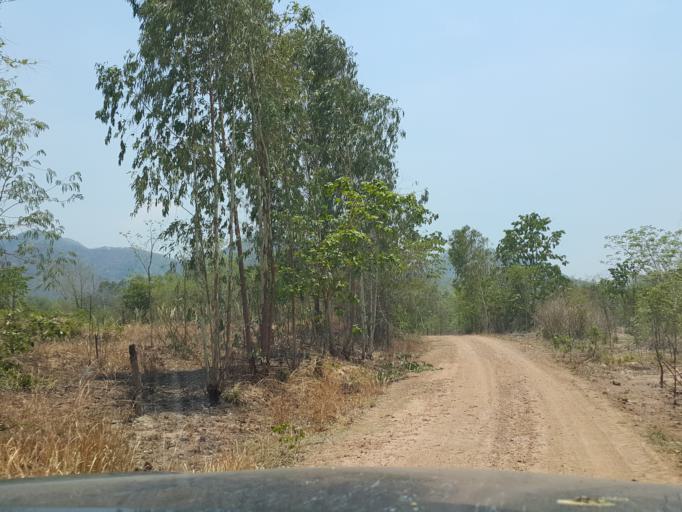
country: TH
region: Lampang
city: Thoen
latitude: 17.6385
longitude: 99.2755
